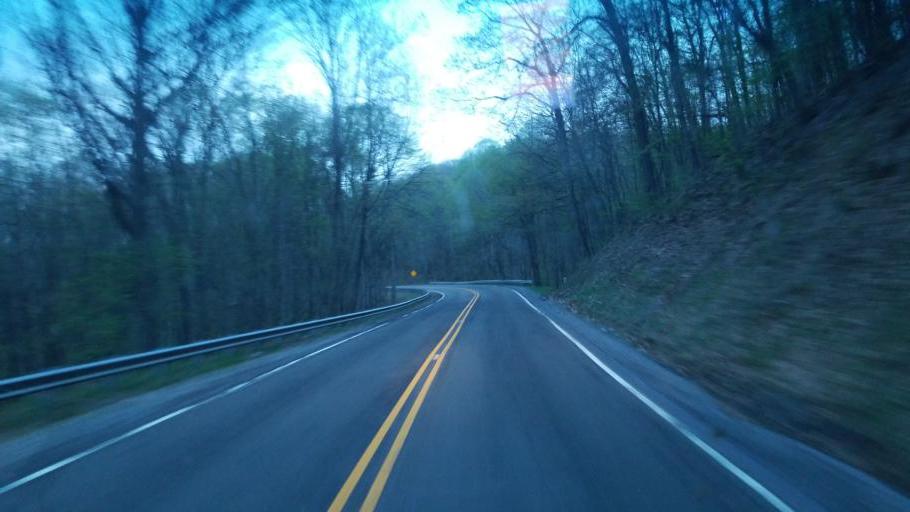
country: US
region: Virginia
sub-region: Smyth County
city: Atkins
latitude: 36.8179
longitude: -81.4322
